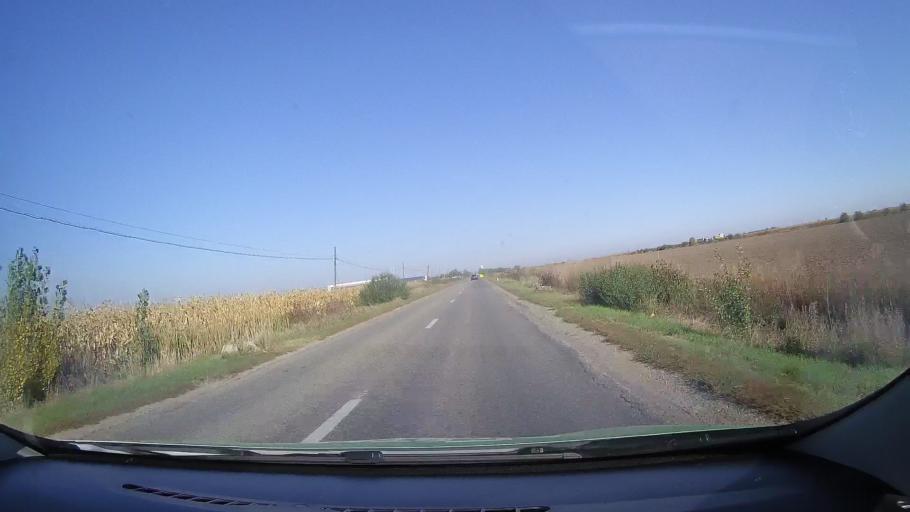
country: RO
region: Satu Mare
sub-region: Oras Tasnad
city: Tasnad
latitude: 47.5015
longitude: 22.5744
